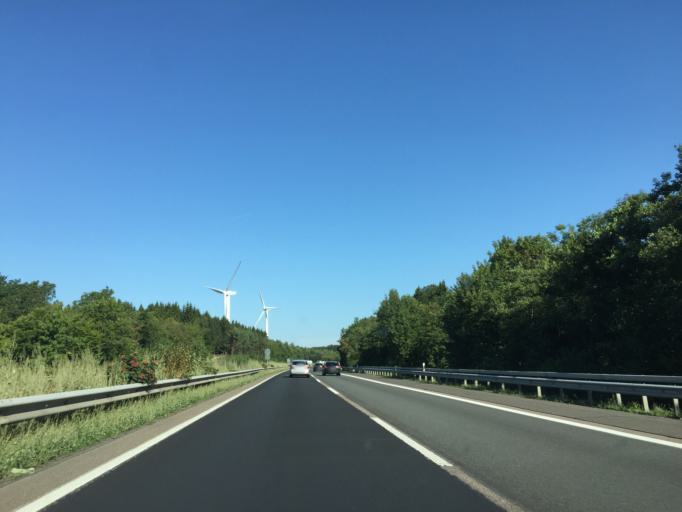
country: DE
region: Rheinland-Pfalz
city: Hungenroth
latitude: 50.1269
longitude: 7.5960
